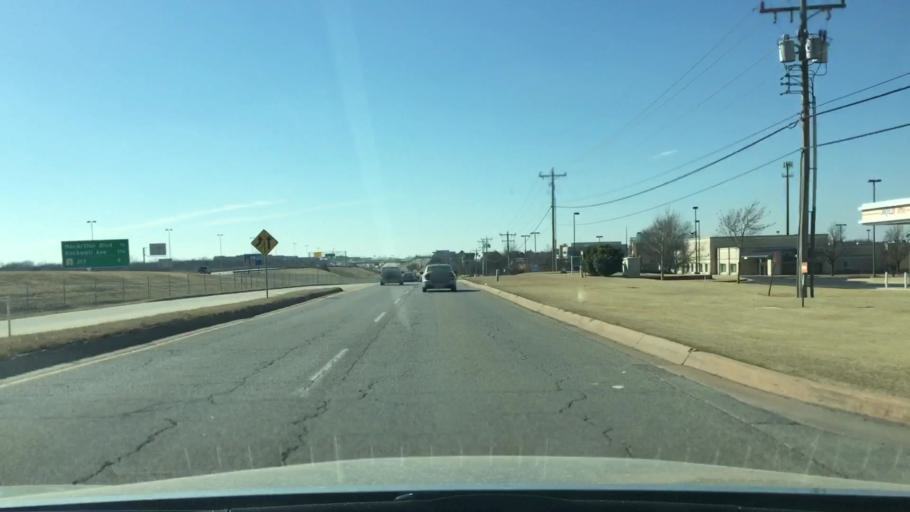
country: US
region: Oklahoma
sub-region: Oklahoma County
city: The Village
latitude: 35.6103
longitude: -97.5983
